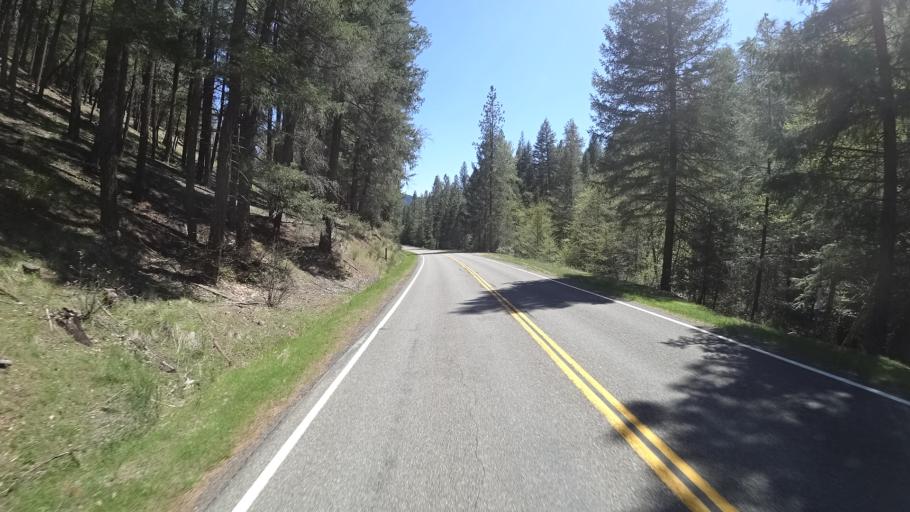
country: US
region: California
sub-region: Trinity County
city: Weaverville
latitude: 40.7667
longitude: -122.8896
